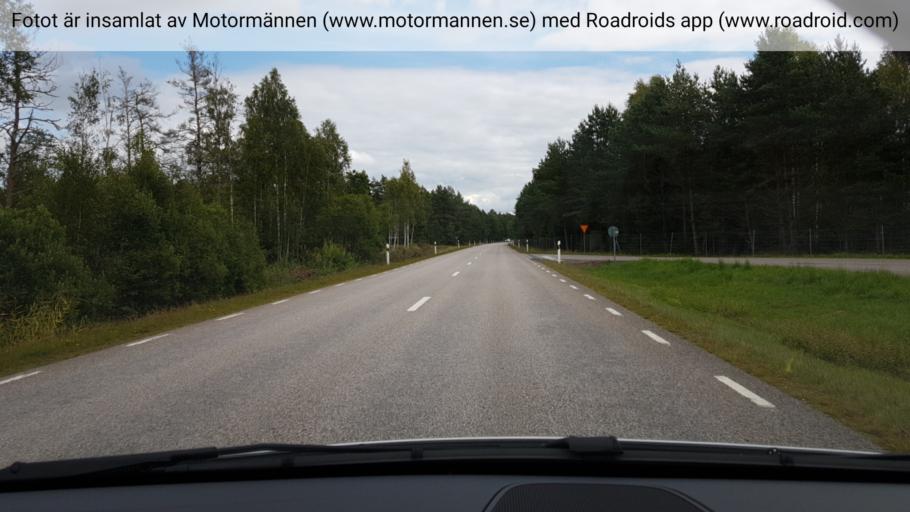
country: SE
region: Vaestra Goetaland
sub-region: Vara Kommun
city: Kvanum
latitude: 58.2138
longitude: 13.2315
